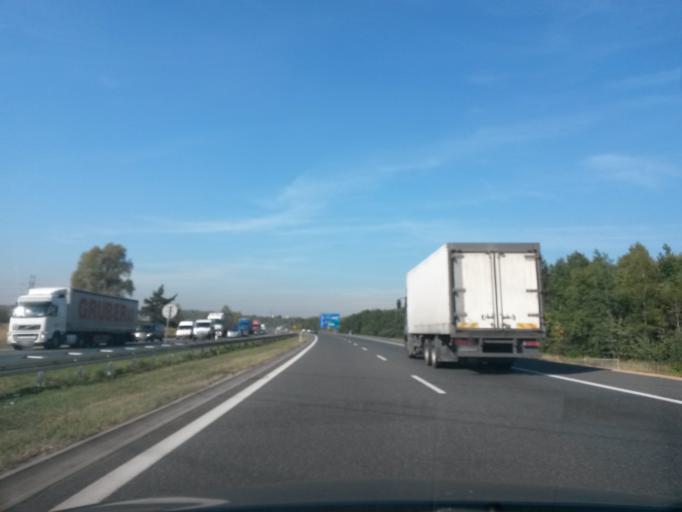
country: PL
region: Silesian Voivodeship
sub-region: Myslowice
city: Myslowice
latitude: 50.1998
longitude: 19.1835
